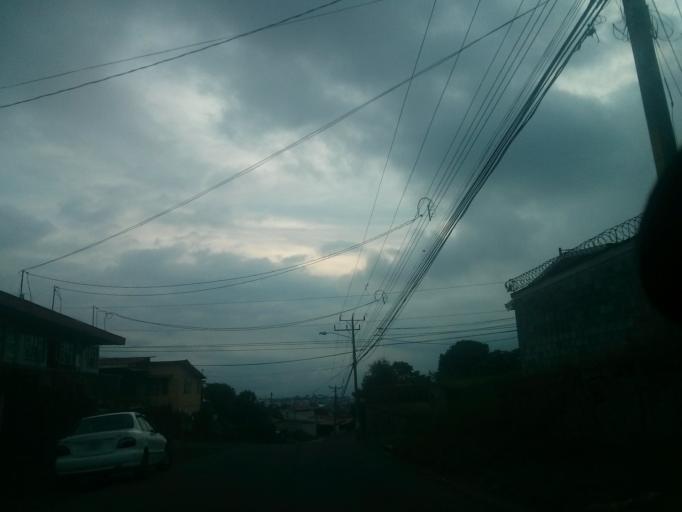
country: CR
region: Heredia
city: San Pablo
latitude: 9.9938
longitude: -84.1022
